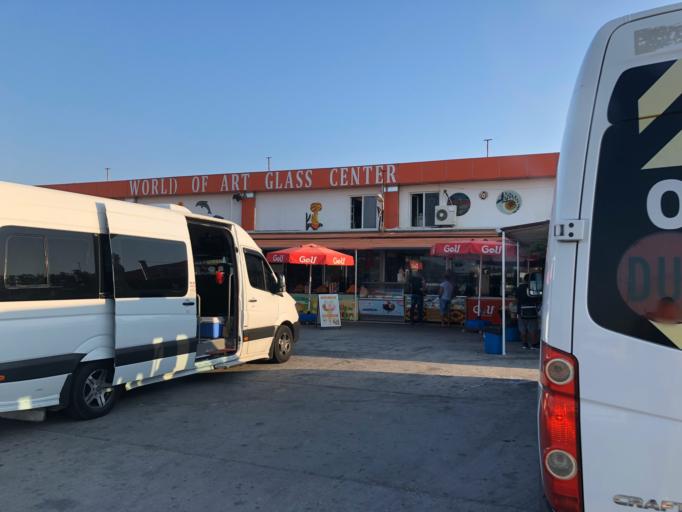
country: TR
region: Antalya
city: Tasagil
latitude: 36.8651
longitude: 31.2739
